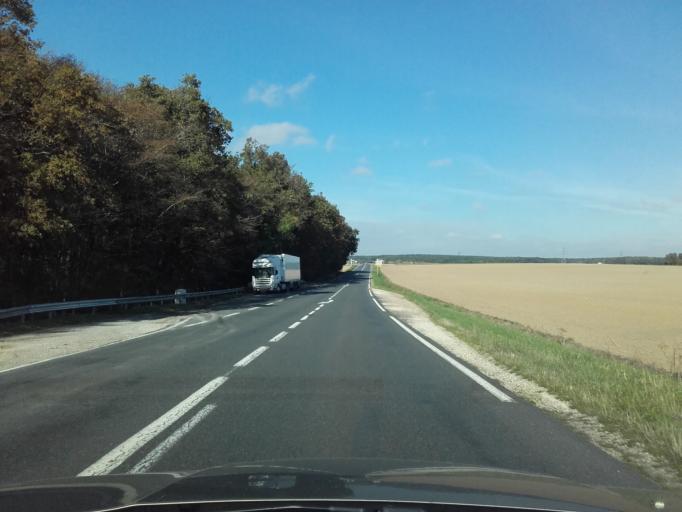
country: FR
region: Centre
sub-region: Departement d'Indre-et-Loire
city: Auzouer-en-Touraine
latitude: 47.5457
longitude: 0.9802
